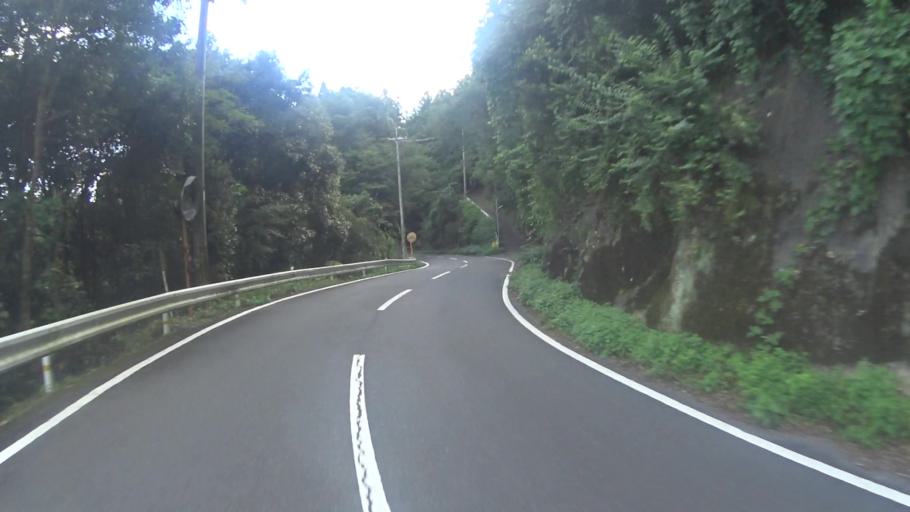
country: JP
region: Mie
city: Ueno-ebisumachi
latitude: 34.7234
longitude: 136.0015
